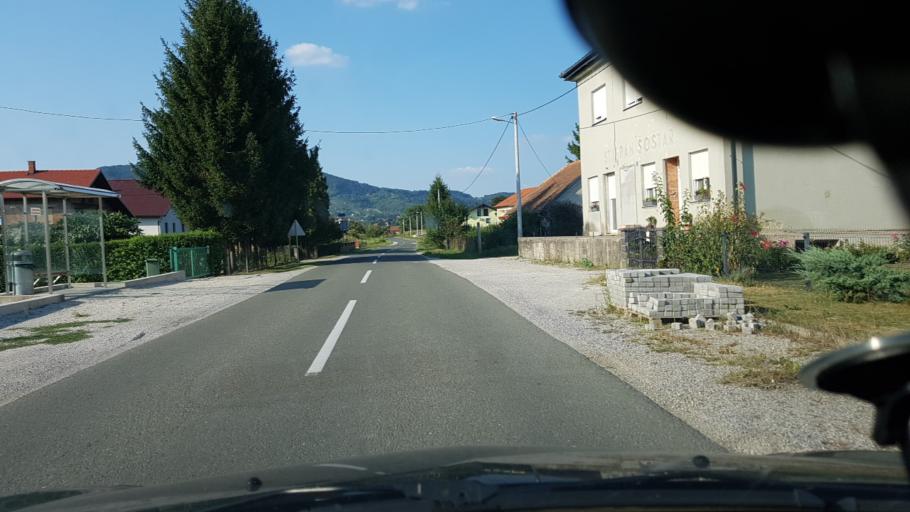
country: SI
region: Bistrica ob Sotli
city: Bistrica ob Sotli
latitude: 46.0261
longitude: 15.7308
